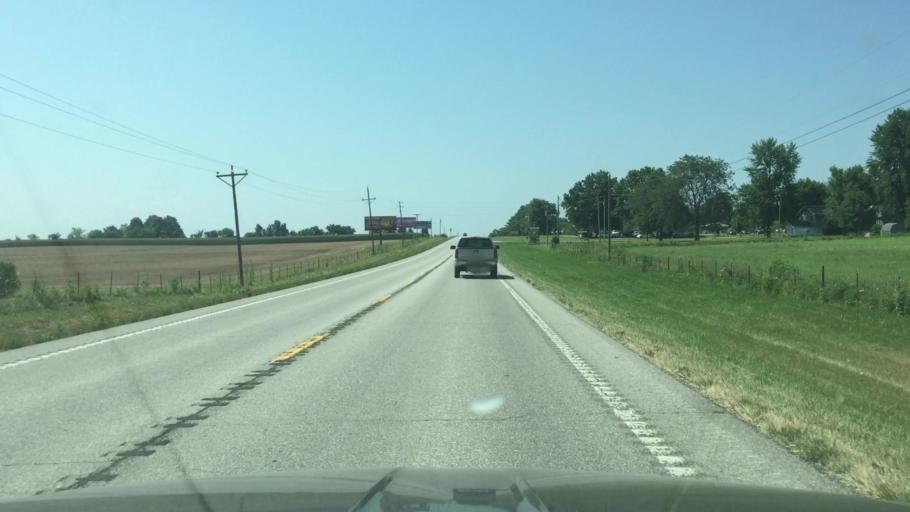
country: US
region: Missouri
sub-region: Morgan County
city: Versailles
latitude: 38.4733
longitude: -92.8087
